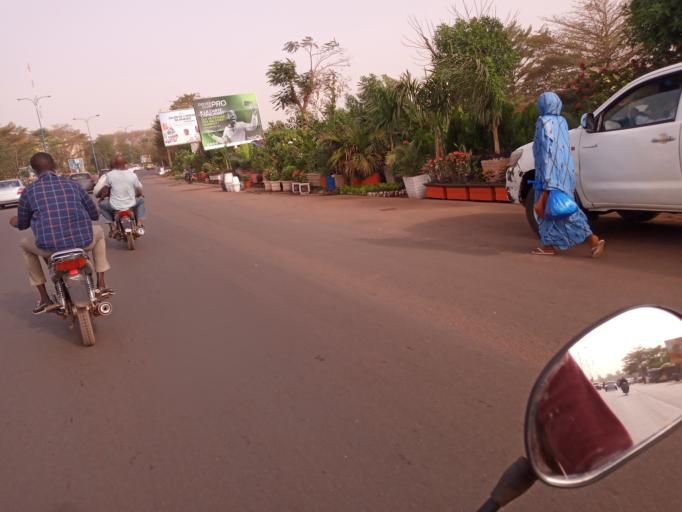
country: ML
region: Bamako
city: Bamako
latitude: 12.6382
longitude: -8.0185
